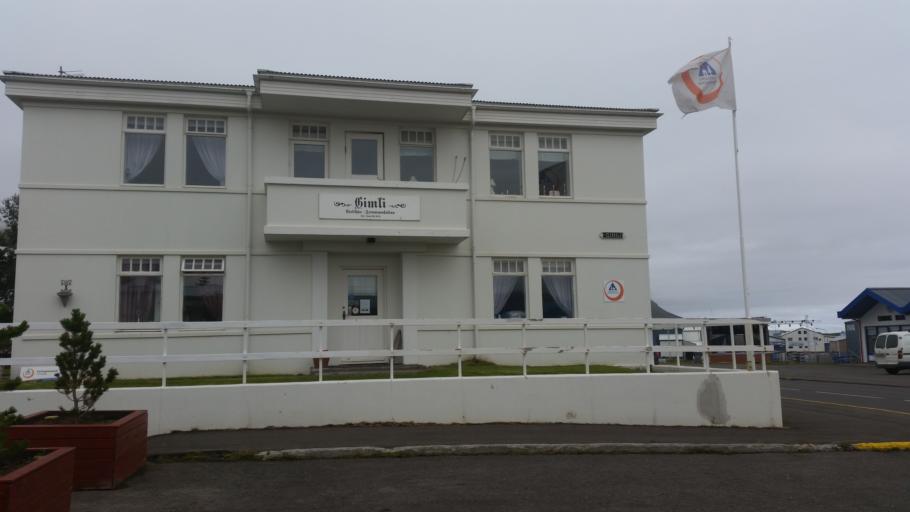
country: IS
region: Northeast
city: Dalvik
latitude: 65.9717
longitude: -18.5303
